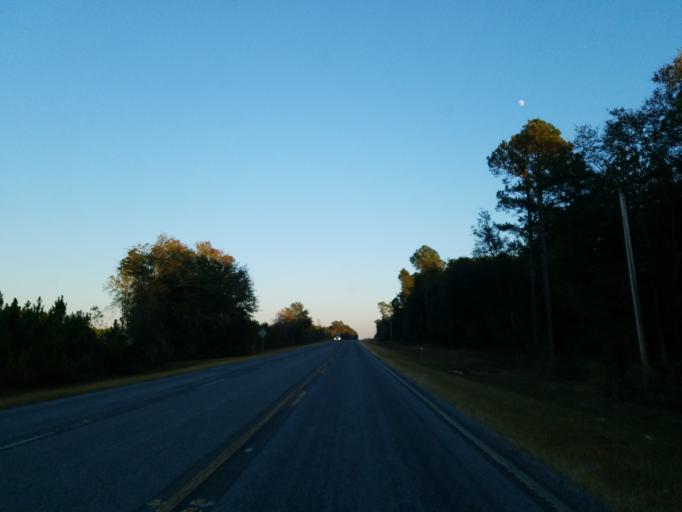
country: US
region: Georgia
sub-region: Ben Hill County
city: Fitzgerald
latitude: 31.7208
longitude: -83.4326
